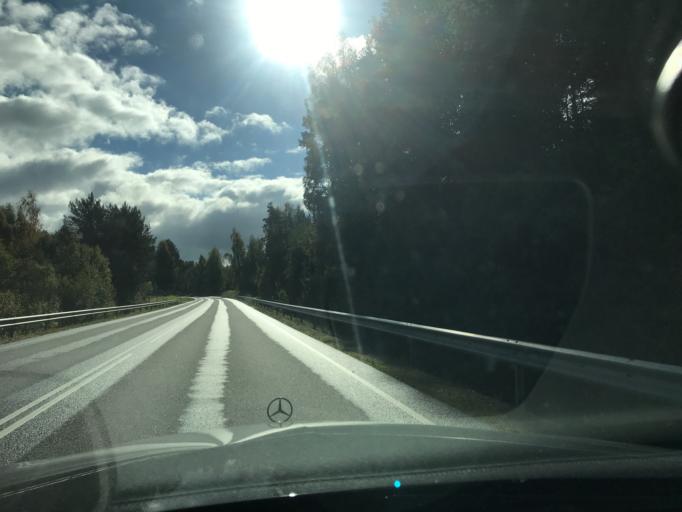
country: EE
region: Vorumaa
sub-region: Voru linn
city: Voru
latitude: 57.7883
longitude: 27.0990
